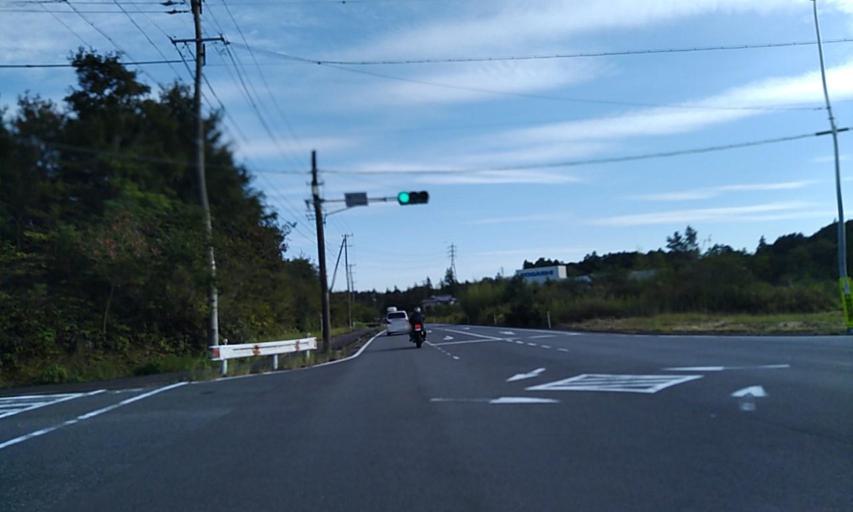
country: JP
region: Mie
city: Toba
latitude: 34.3545
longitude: 136.8071
